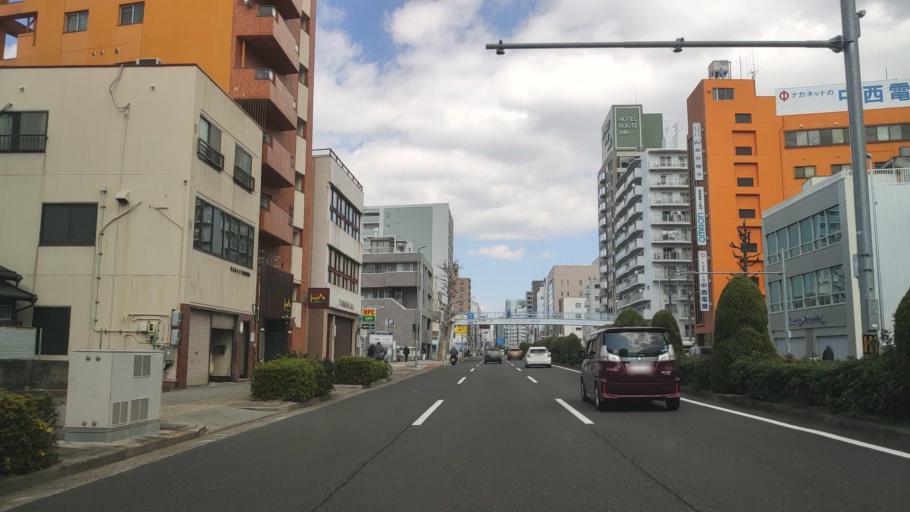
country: JP
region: Aichi
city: Nagoya-shi
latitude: 35.1531
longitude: 136.9050
